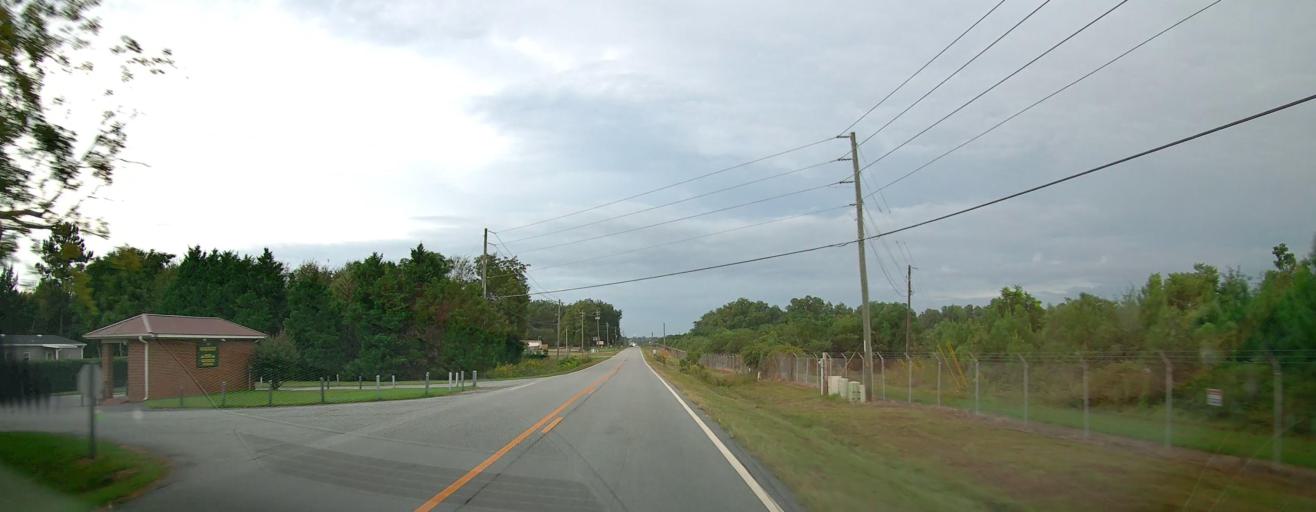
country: US
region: Georgia
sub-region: Peach County
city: Byron
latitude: 32.6514
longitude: -83.7273
